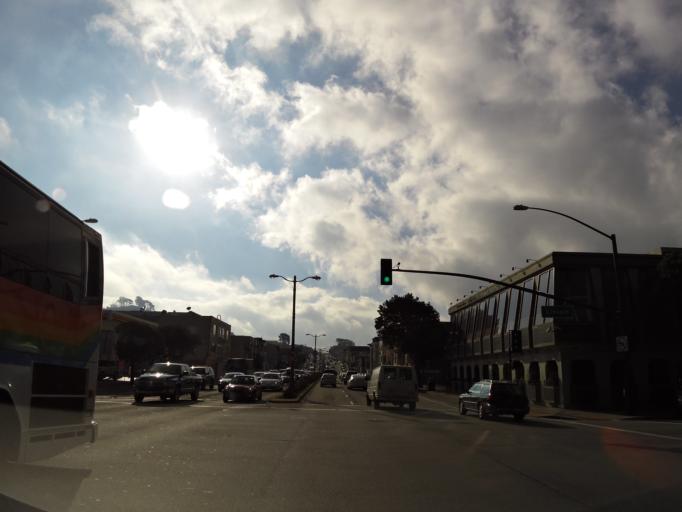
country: US
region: California
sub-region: San Francisco County
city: San Francisco
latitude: 37.7656
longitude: -122.4774
